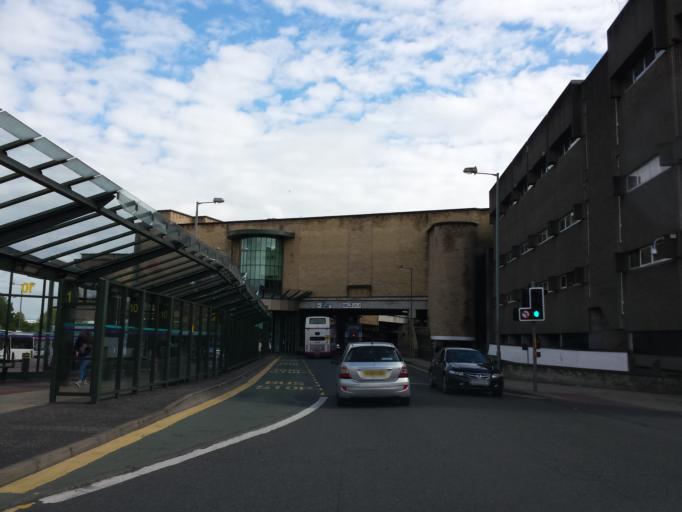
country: GB
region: Scotland
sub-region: Stirling
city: Stirling
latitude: 56.1185
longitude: -3.9349
